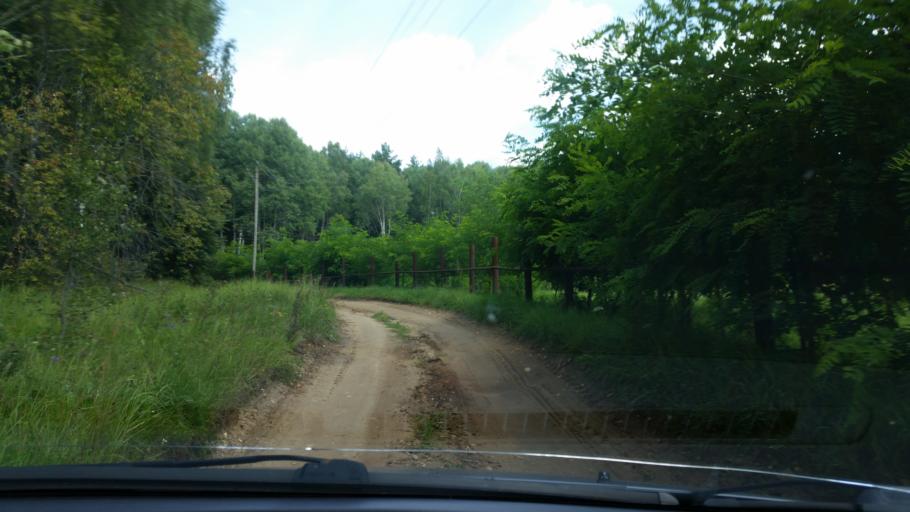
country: RU
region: Moskovskaya
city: Pushchino
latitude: 54.9144
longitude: 37.7334
